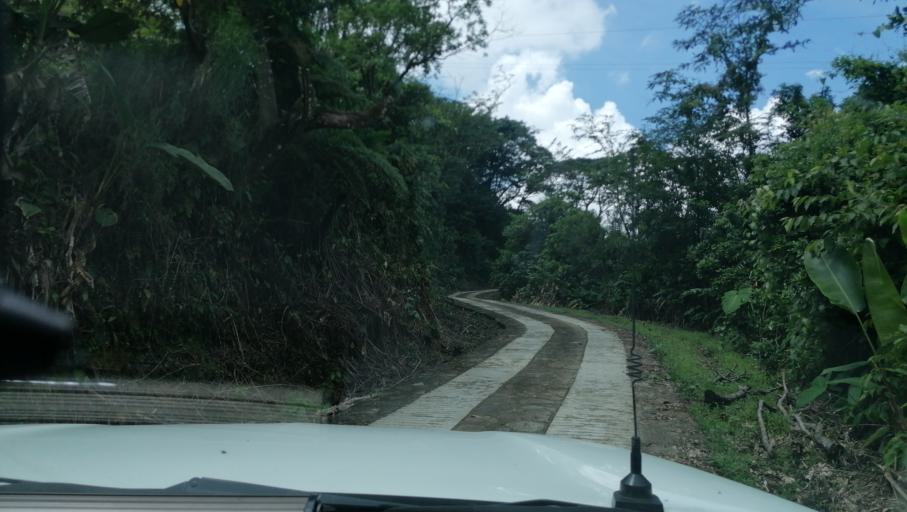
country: MX
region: Chiapas
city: Pichucalco
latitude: 17.4498
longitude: -93.1991
